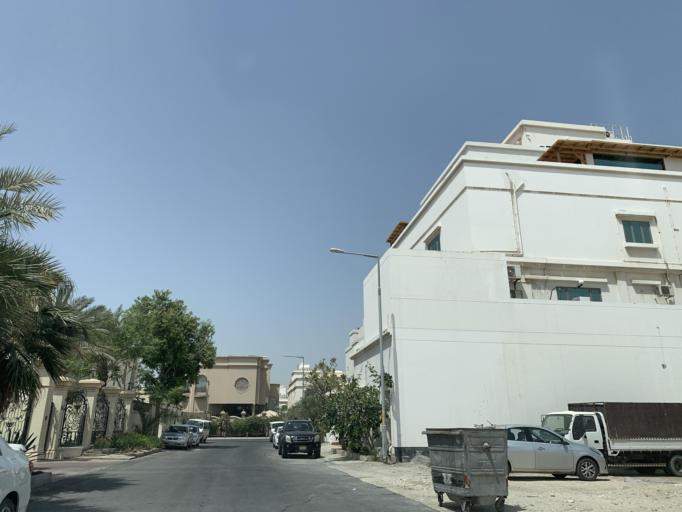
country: BH
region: Manama
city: Manama
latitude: 26.2004
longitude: 50.5662
